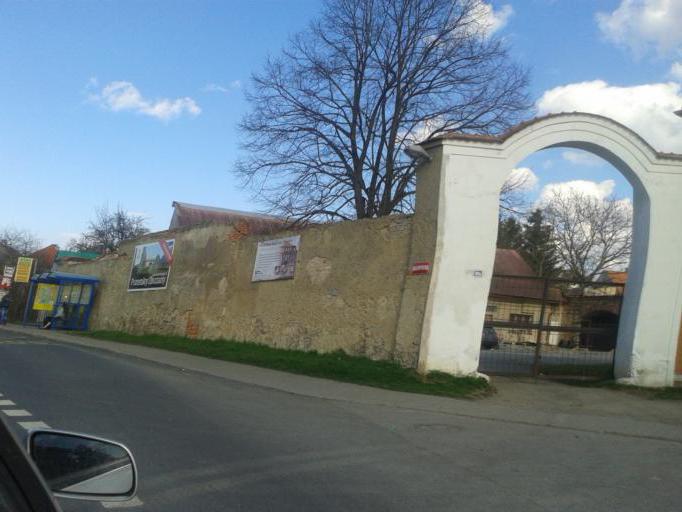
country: CZ
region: Central Bohemia
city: Rudna
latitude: 50.0267
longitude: 14.2123
